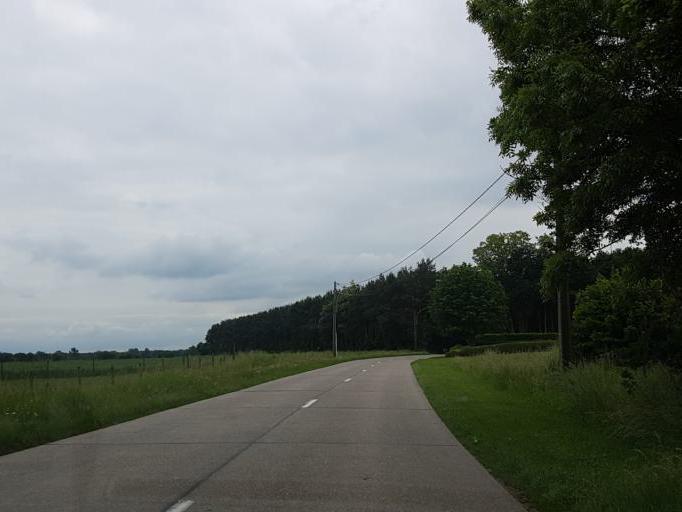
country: BE
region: Flanders
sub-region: Provincie Antwerpen
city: Rijkevorsel
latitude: 51.3737
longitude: 4.8045
